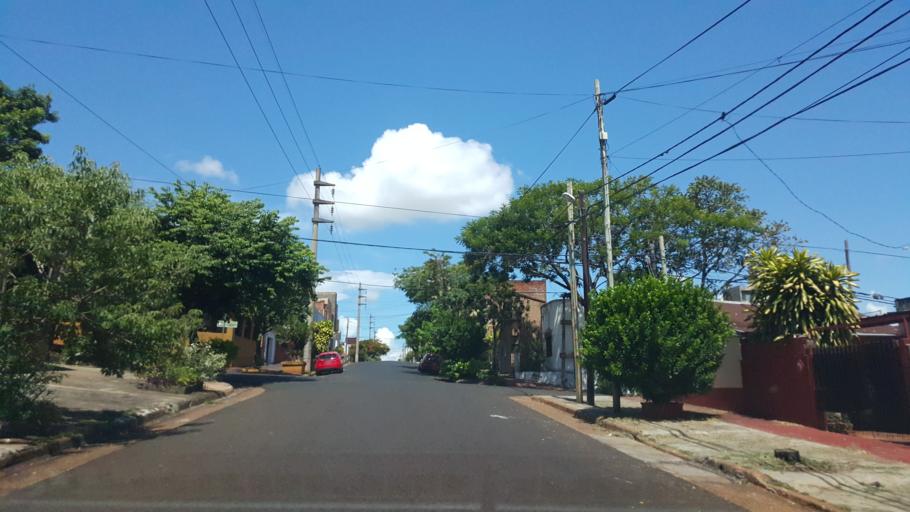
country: AR
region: Misiones
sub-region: Departamento de Capital
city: Posadas
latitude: -27.3586
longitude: -55.8982
